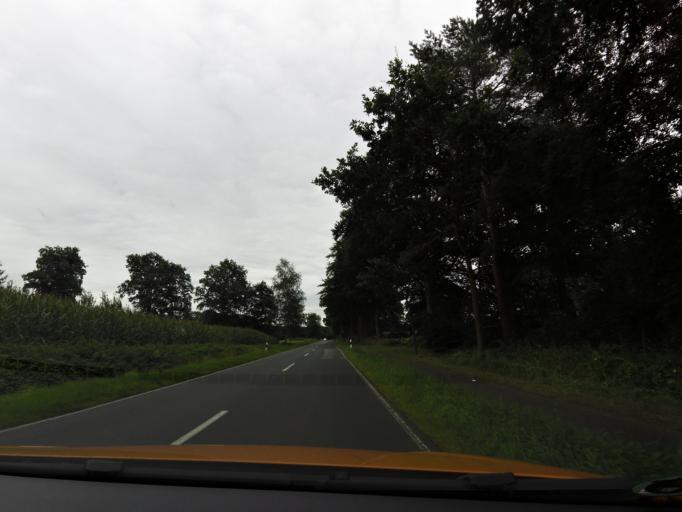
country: DE
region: Lower Saxony
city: Wiefelstede
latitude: 53.2076
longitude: 8.1060
